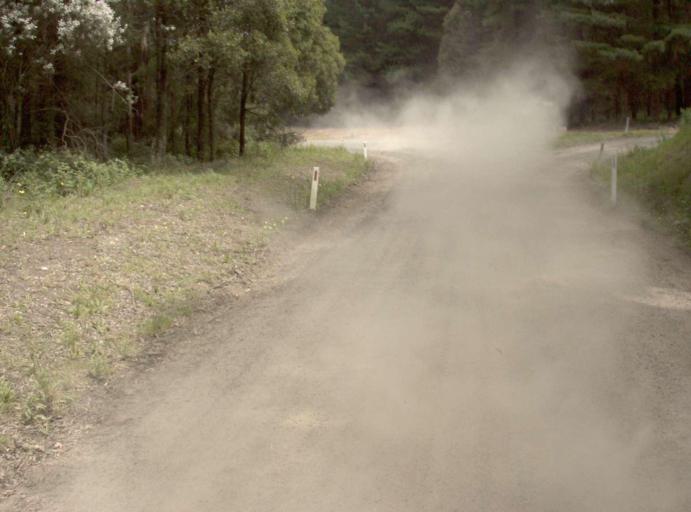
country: AU
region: Victoria
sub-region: Latrobe
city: Traralgon
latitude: -38.3796
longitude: 146.6680
